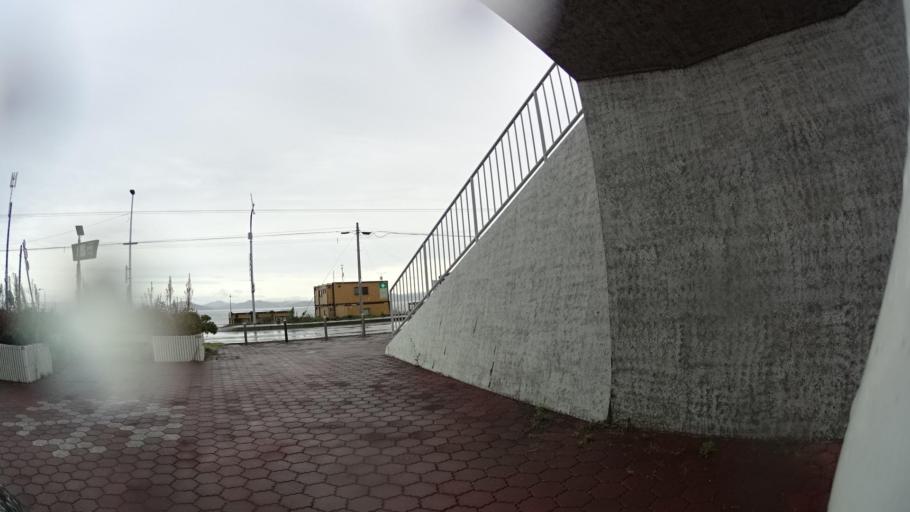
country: JP
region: Hokkaido
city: Mombetsu
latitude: 44.3341
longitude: 143.4874
